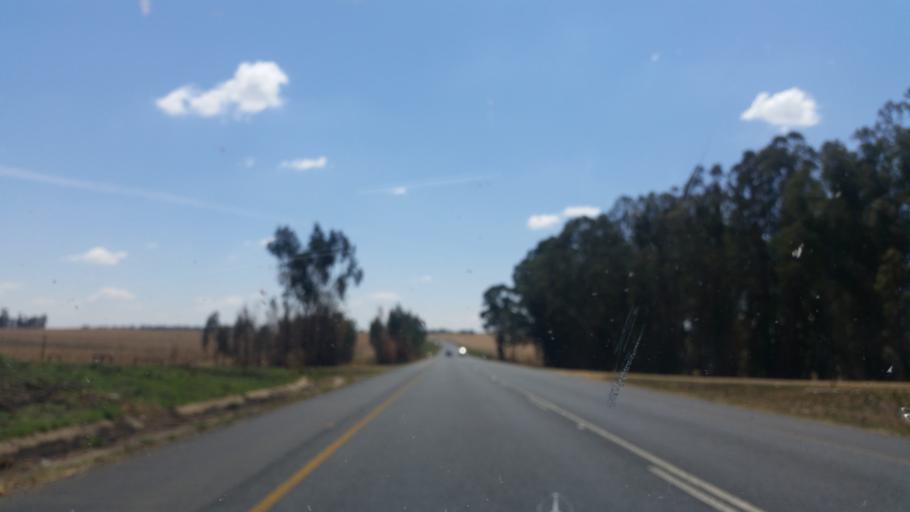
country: ZA
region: Orange Free State
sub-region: Thabo Mofutsanyana District Municipality
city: Reitz
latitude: -28.0934
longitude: 28.6551
